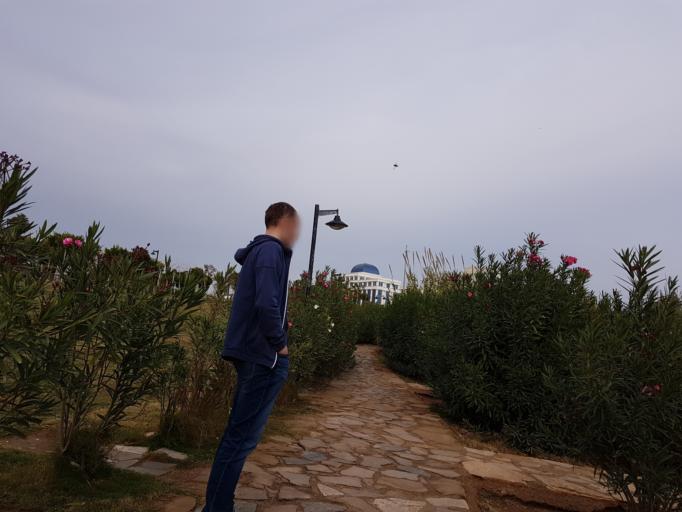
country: TR
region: Antalya
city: Antalya
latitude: 36.8505
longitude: 30.7825
